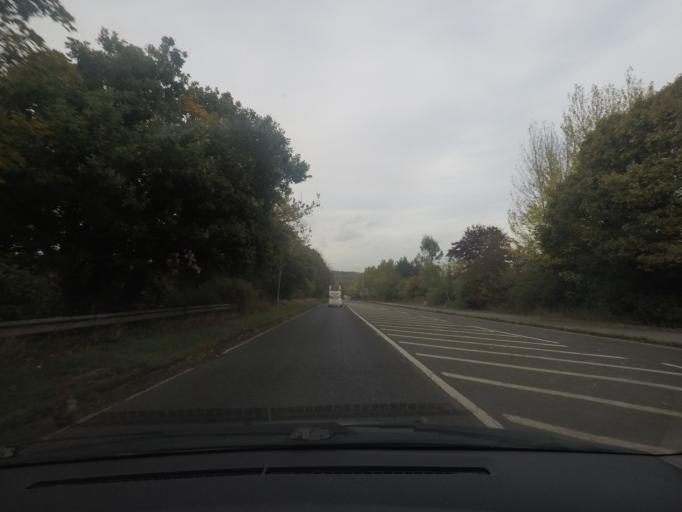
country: GB
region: England
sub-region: Barnsley
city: Wortley
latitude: 53.4722
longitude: -1.5051
